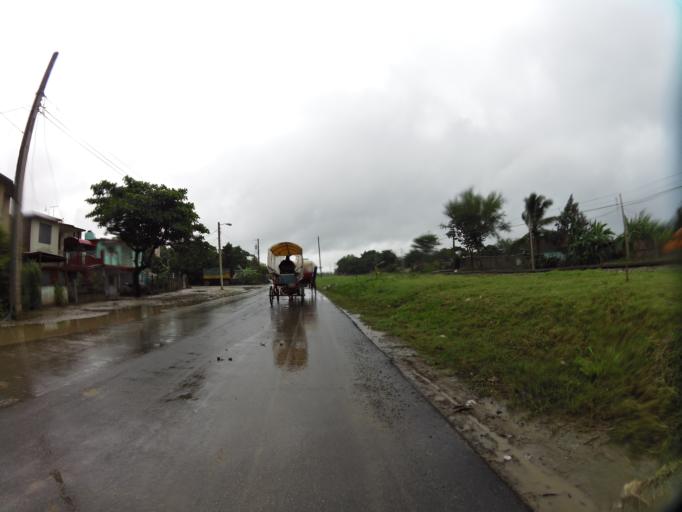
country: CU
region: Las Tunas
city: Las Tunas
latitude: 20.9639
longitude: -76.9378
